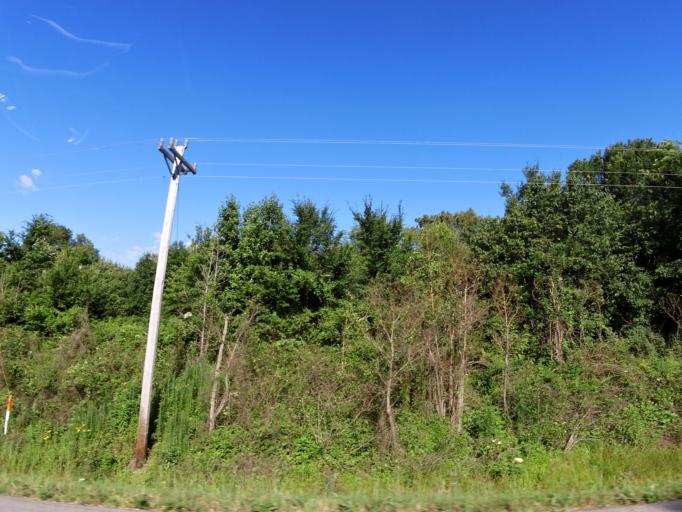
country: US
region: Missouri
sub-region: Butler County
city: Poplar Bluff
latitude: 36.6529
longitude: -90.5202
